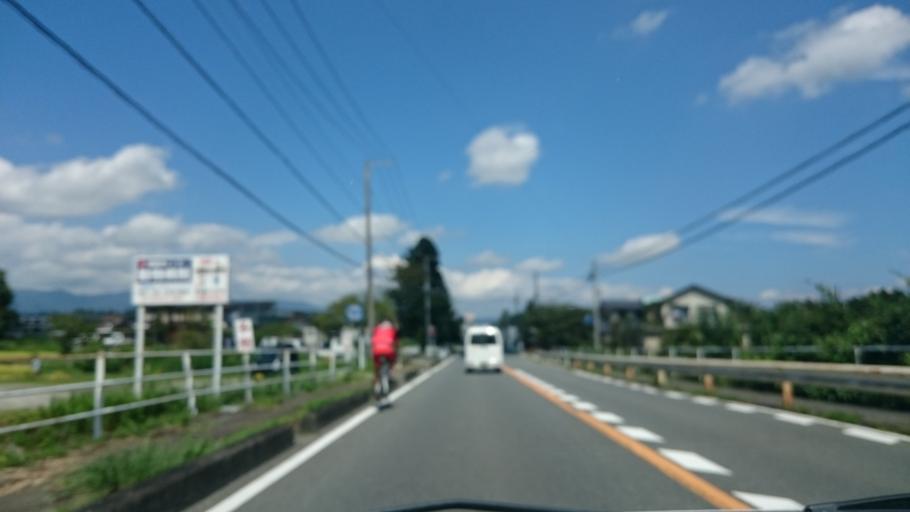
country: JP
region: Shizuoka
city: Gotemba
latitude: 35.2797
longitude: 138.9268
